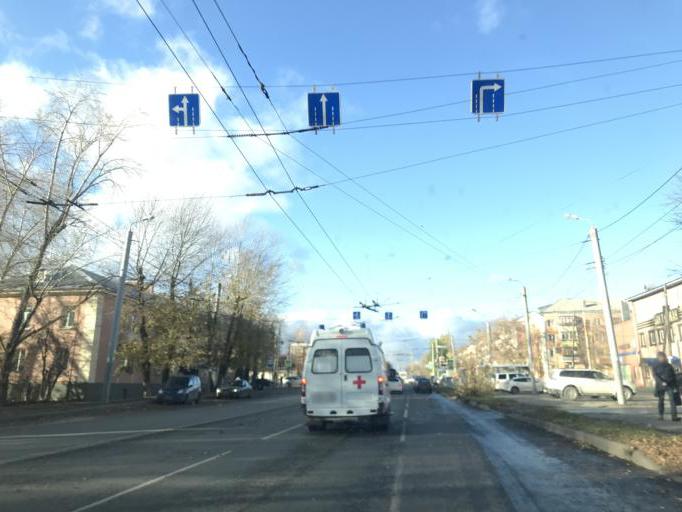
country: RU
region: Chelyabinsk
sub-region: Gorod Chelyabinsk
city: Chelyabinsk
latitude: 55.1803
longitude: 61.4466
